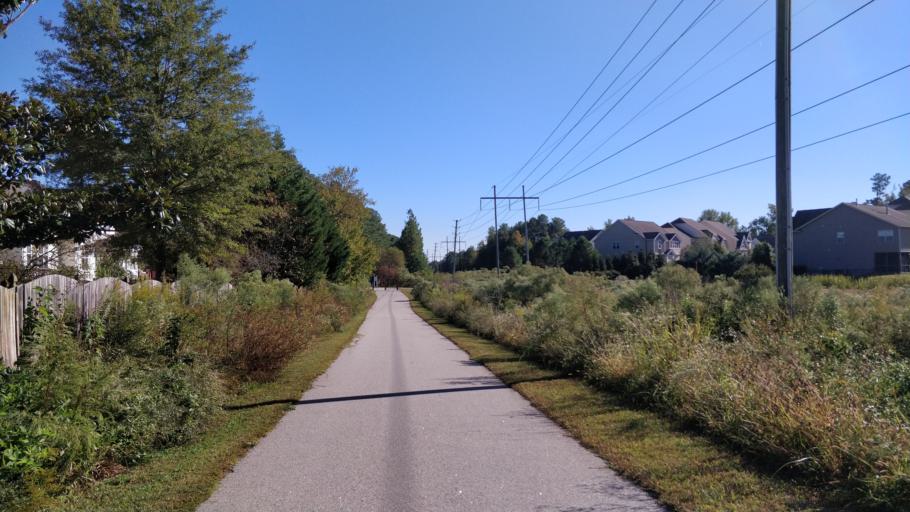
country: US
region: North Carolina
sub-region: Wake County
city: Morrisville
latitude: 35.8365
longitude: -78.8435
